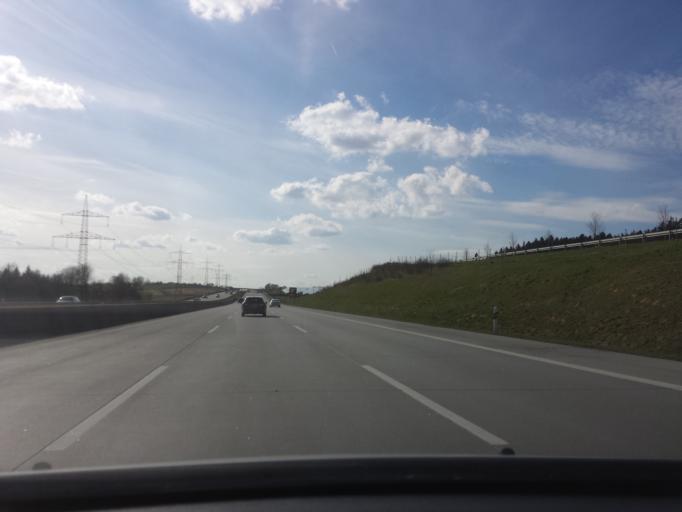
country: DE
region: Bavaria
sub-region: Swabia
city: Dasing
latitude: 48.4002
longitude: 11.0073
